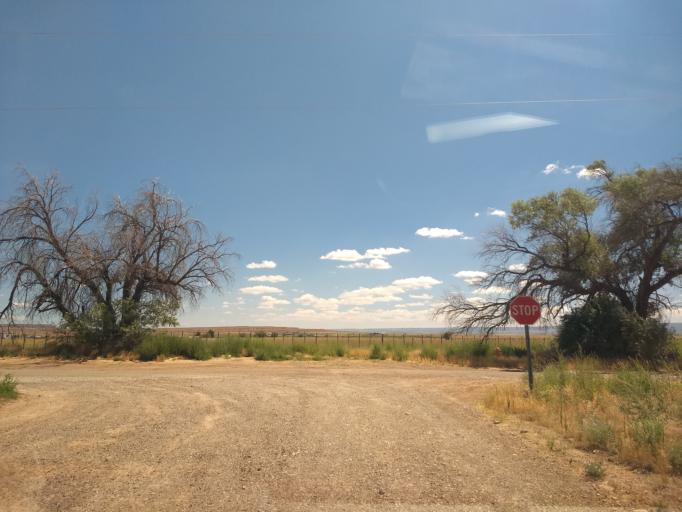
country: US
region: Arizona
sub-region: Coconino County
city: Fredonia
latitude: 36.9326
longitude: -112.5355
